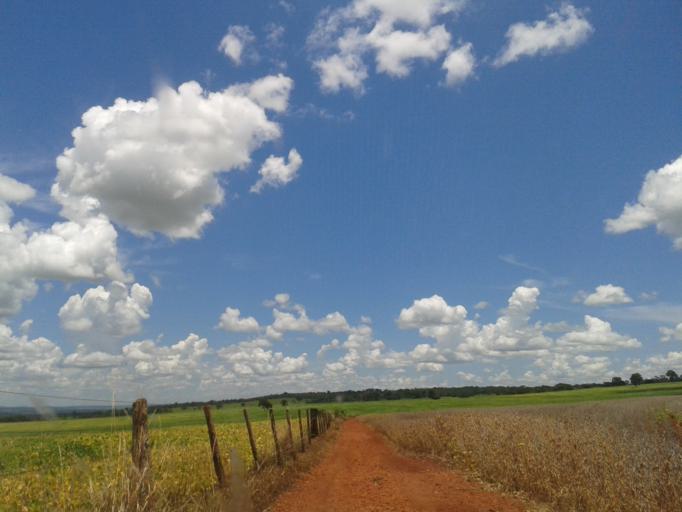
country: BR
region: Minas Gerais
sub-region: Capinopolis
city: Capinopolis
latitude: -18.7624
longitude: -49.7932
